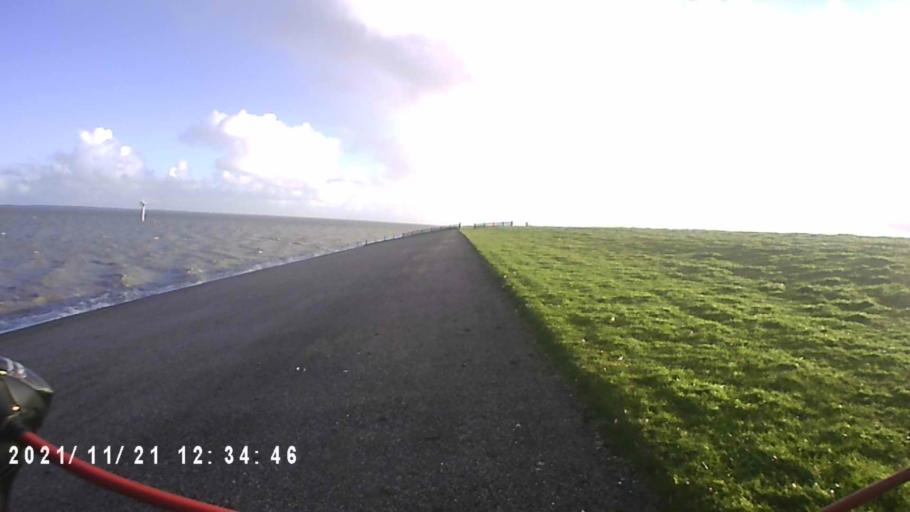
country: NL
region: Friesland
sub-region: Gemeente Dongeradeel
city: Anjum
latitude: 53.4061
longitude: 6.0600
